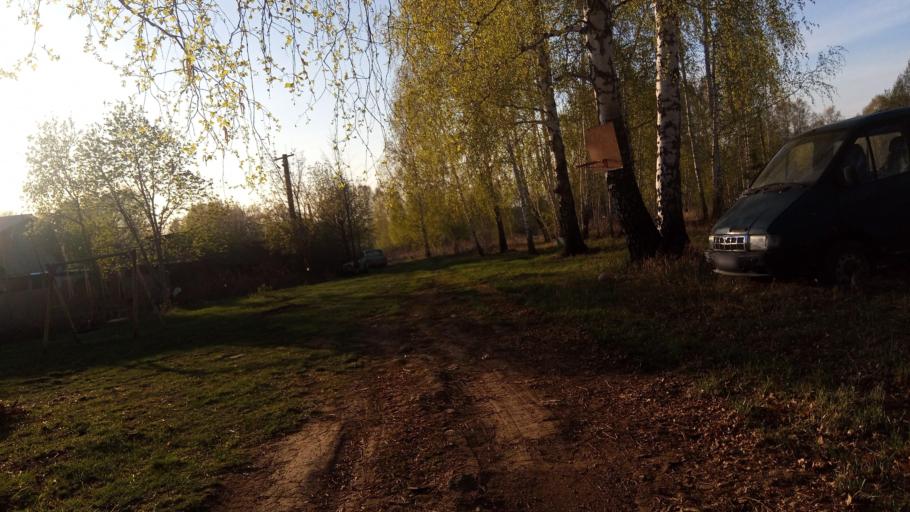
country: RU
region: Chelyabinsk
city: Timiryazevskiy
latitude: 54.9934
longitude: 60.8451
